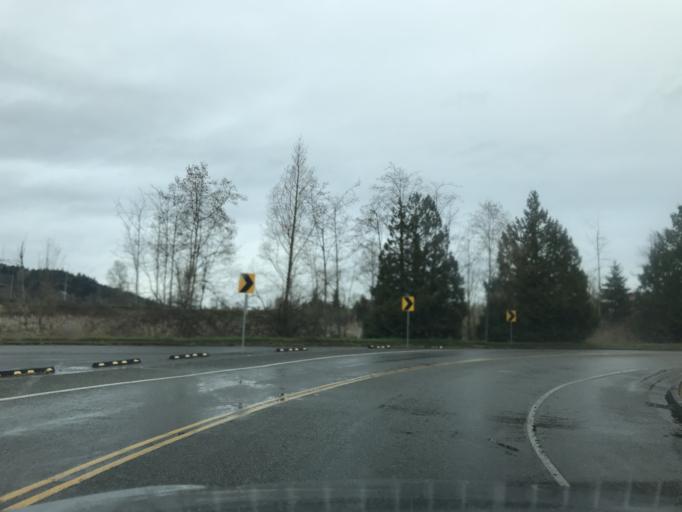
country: US
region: Washington
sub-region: King County
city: Algona
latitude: 47.2933
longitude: -122.2551
